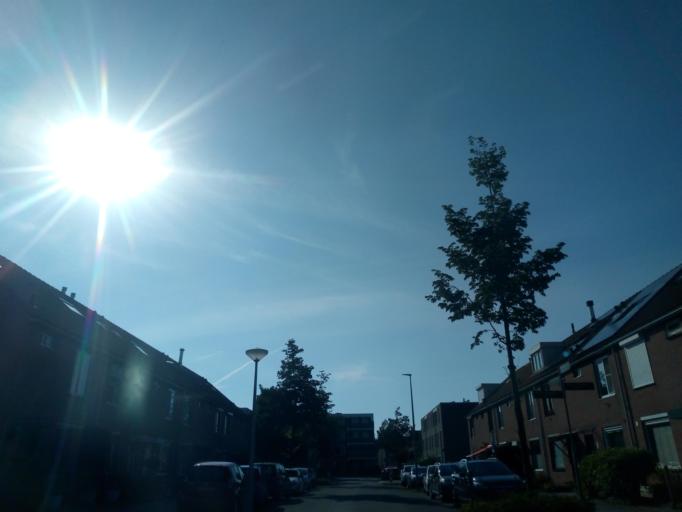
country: NL
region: South Holland
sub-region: Gemeente Alphen aan den Rijn
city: Alphen aan den Rijn
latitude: 52.1547
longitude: 4.6536
